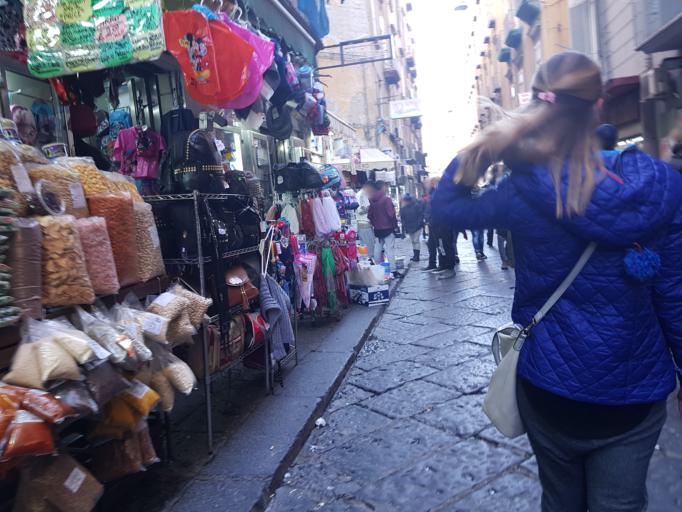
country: IT
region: Campania
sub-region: Provincia di Napoli
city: Napoli
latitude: 40.8451
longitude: 14.2484
